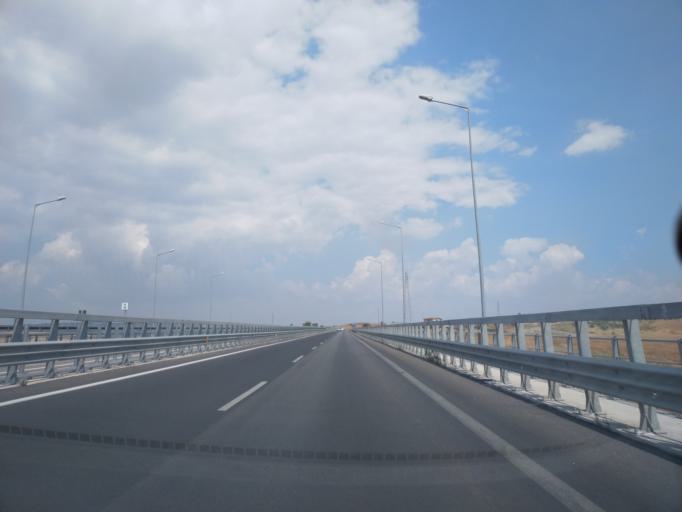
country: IT
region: Sicily
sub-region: Agrigento
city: Favara
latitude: 37.3474
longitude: 13.6546
